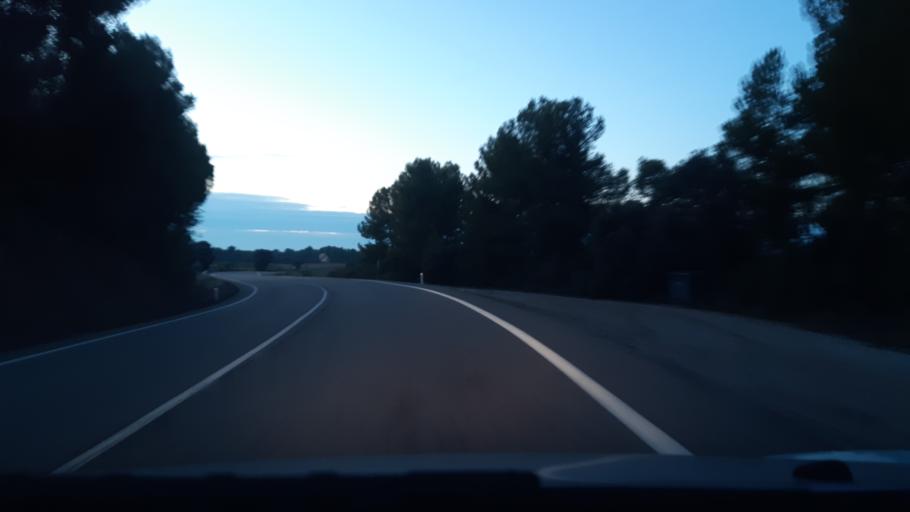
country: ES
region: Aragon
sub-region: Provincia de Teruel
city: Lledo
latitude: 40.9580
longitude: 0.2169
